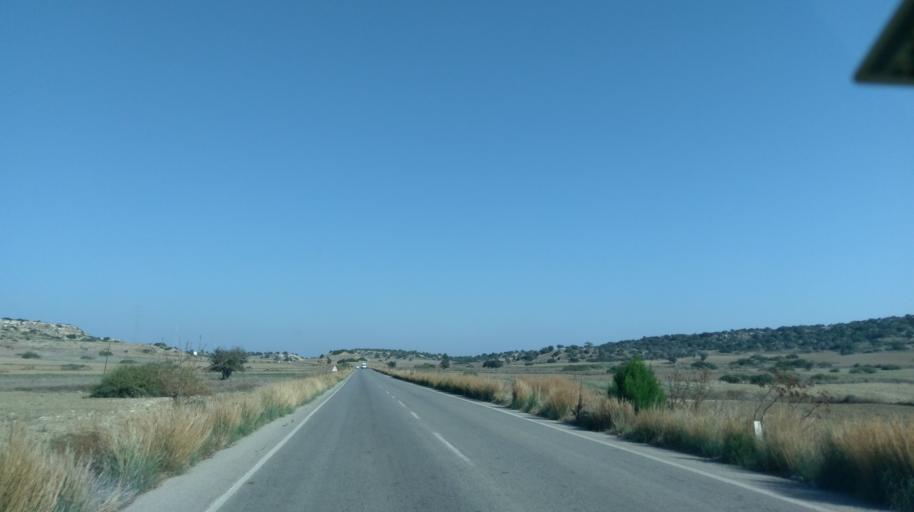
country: CY
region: Ammochostos
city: Leonarisso
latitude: 35.3838
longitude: 34.0468
